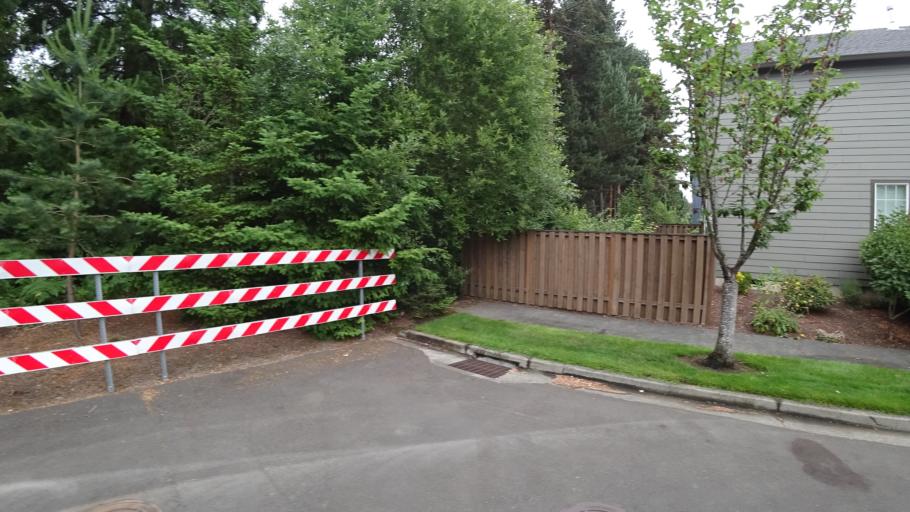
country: US
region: Oregon
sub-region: Washington County
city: Hillsboro
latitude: 45.4944
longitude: -122.9376
